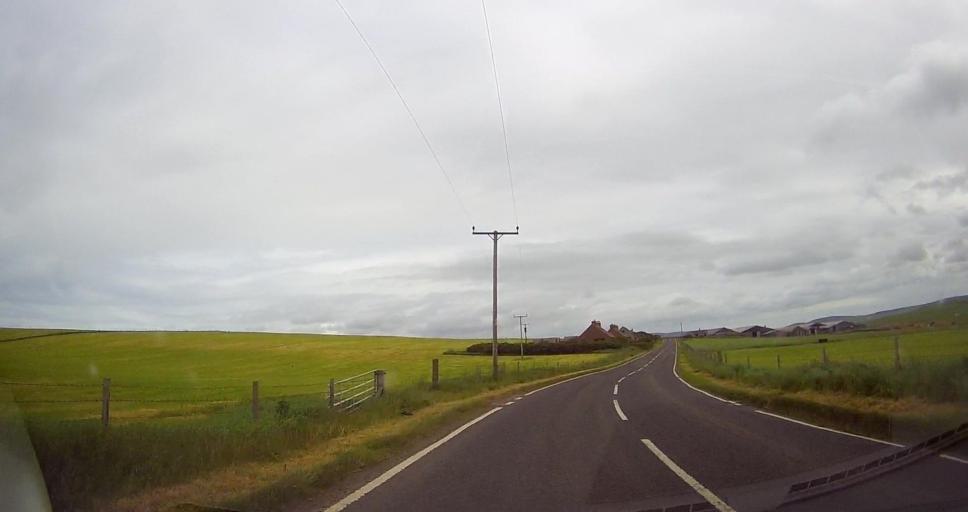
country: GB
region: Scotland
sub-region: Orkney Islands
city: Stromness
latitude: 58.9772
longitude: -3.2707
